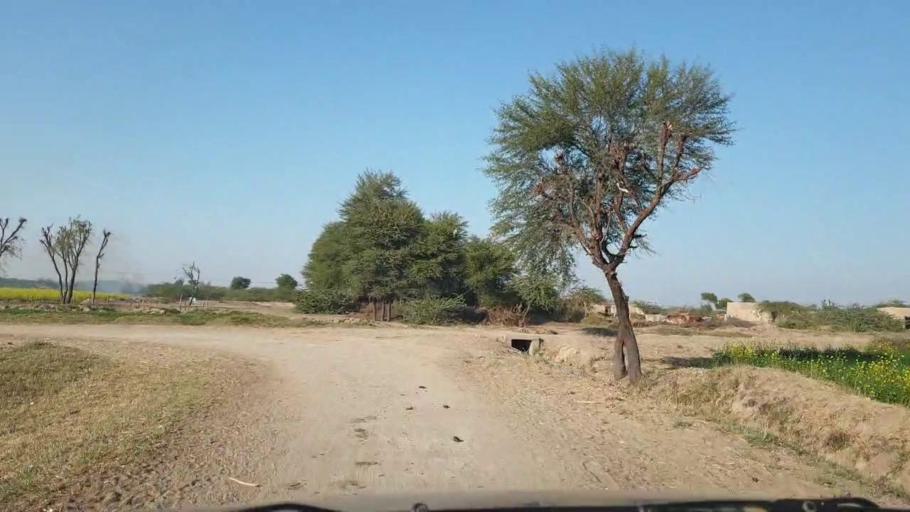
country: PK
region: Sindh
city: Khadro
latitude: 26.2155
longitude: 68.7541
